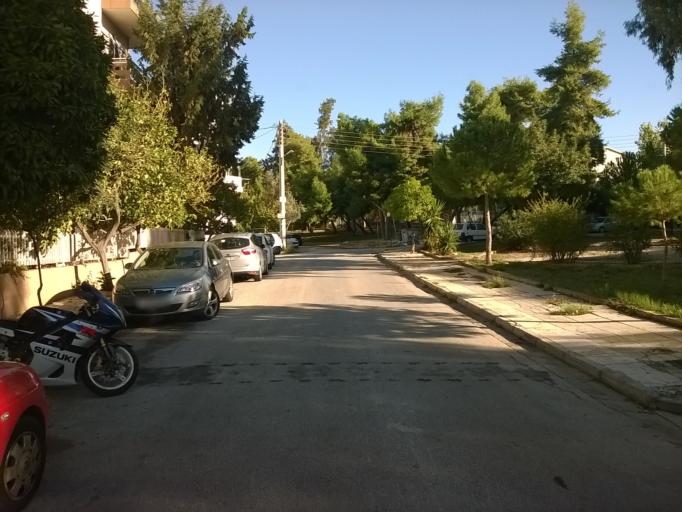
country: GR
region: Attica
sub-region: Nomarchia Athinas
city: Agios Dimitrios
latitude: 37.9198
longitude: 23.7389
